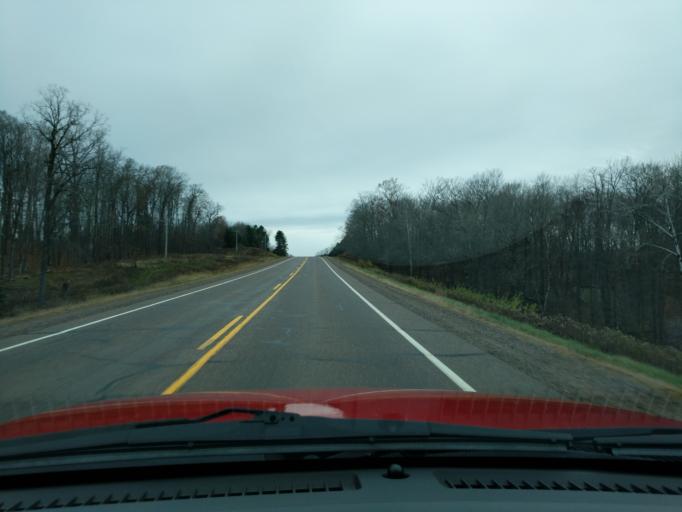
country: US
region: Wisconsin
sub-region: Washburn County
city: Spooner
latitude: 45.8142
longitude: -91.8096
